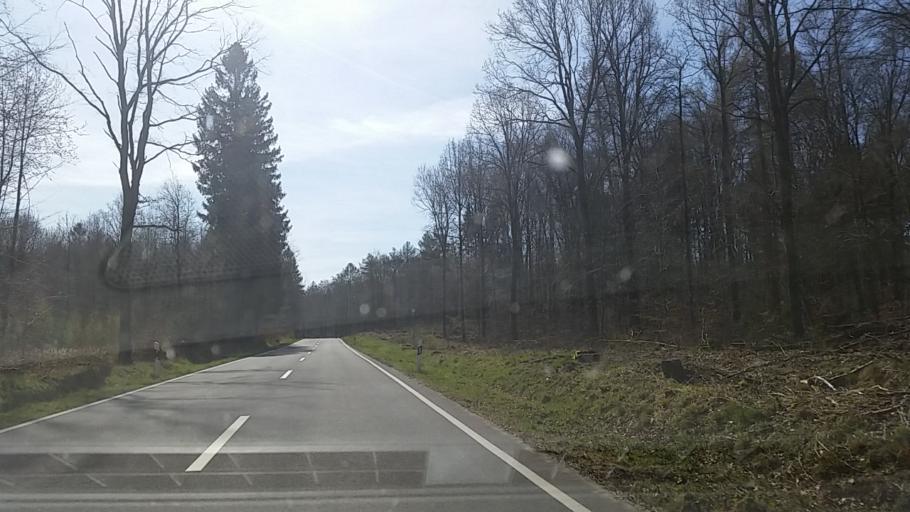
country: DE
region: Lower Saxony
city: Warberg
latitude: 52.1615
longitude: 10.9094
